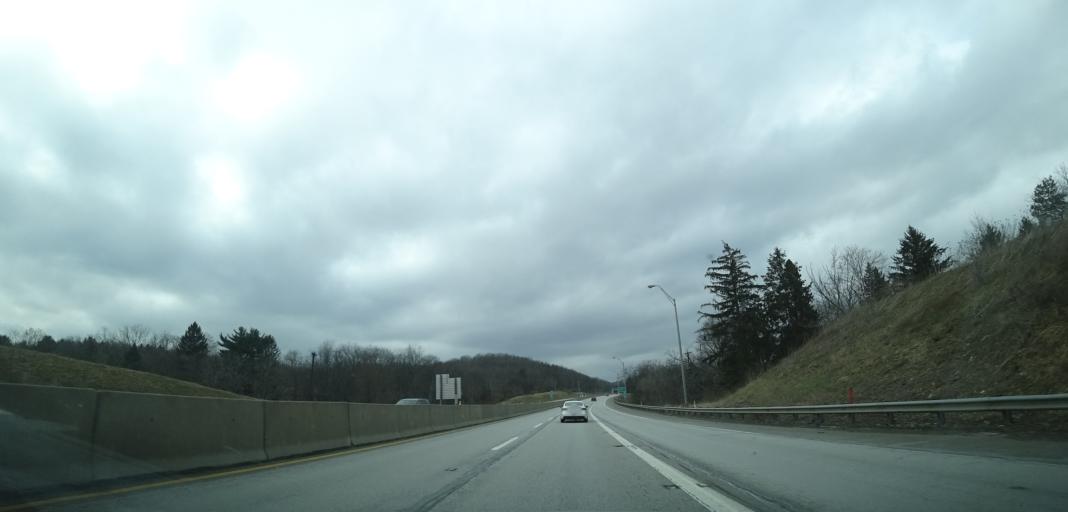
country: US
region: Pennsylvania
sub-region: Allegheny County
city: Gibsonia
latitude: 40.6095
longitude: -79.9485
